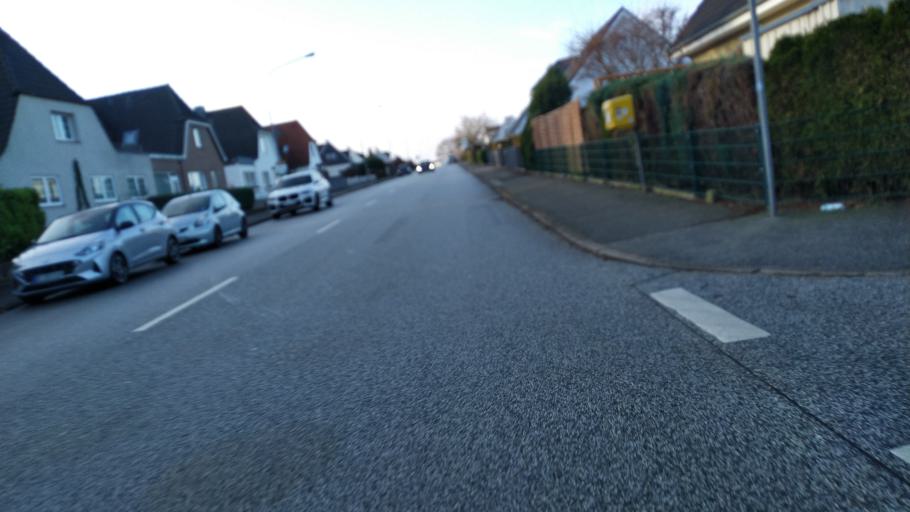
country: DE
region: Schleswig-Holstein
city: Travemuende
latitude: 53.9580
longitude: 10.8527
